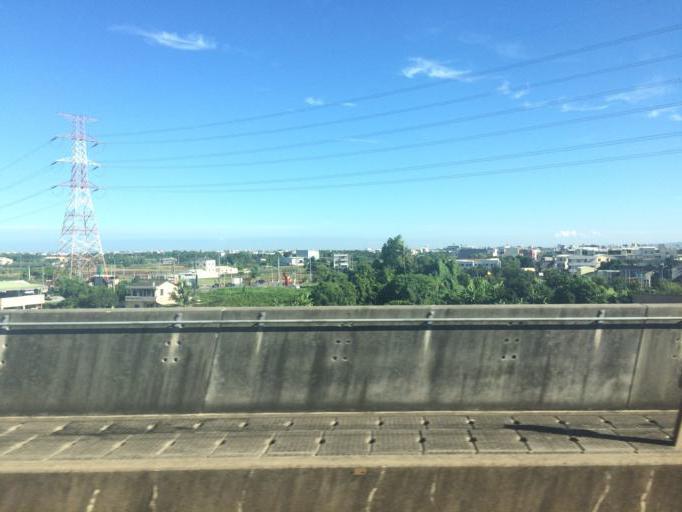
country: TW
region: Taiwan
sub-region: Nantou
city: Nantou
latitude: 23.8825
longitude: 120.5884
